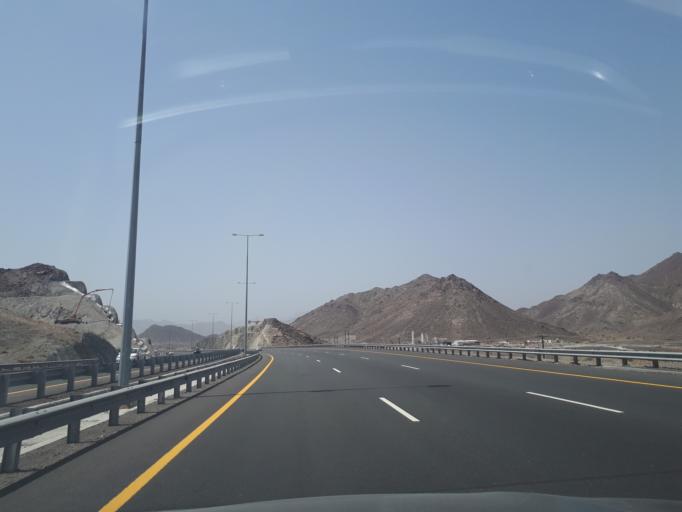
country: OM
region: Muhafazat ad Dakhiliyah
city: Bidbid
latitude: 23.3547
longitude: 58.0910
